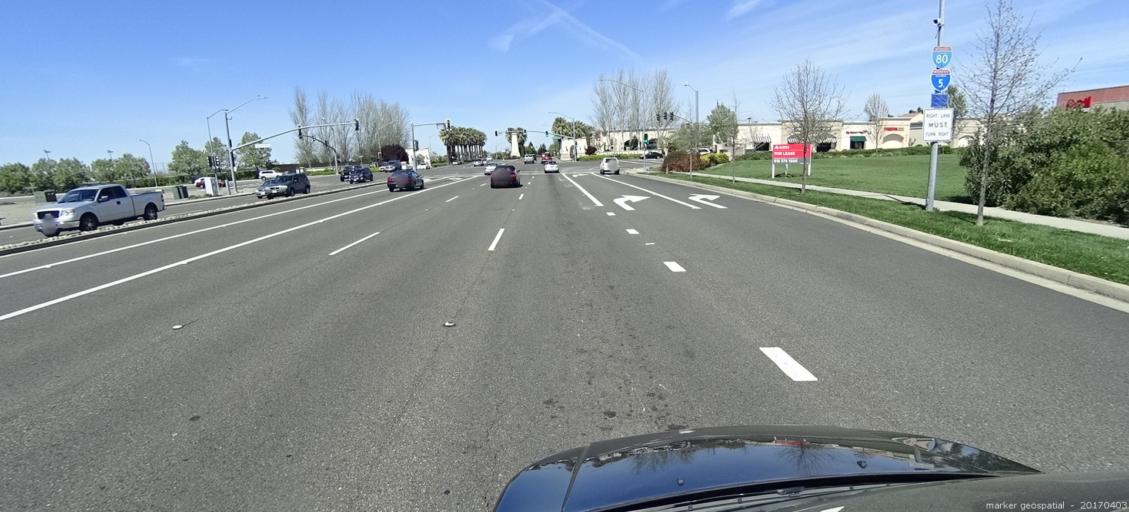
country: US
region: California
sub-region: Sacramento County
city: Rio Linda
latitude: 38.6551
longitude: -121.5119
